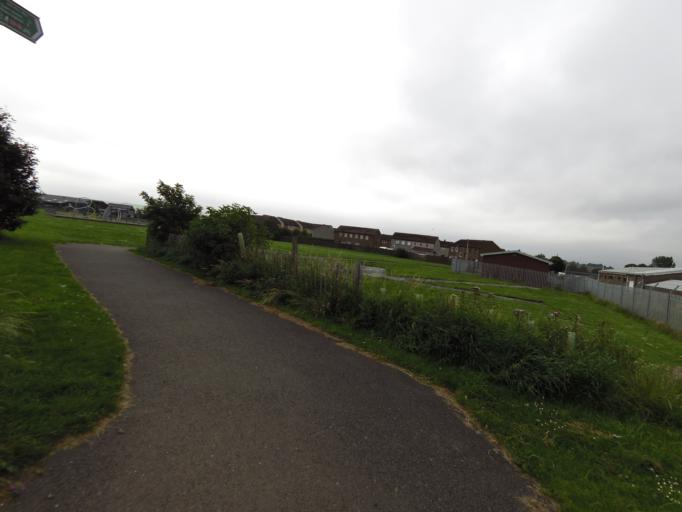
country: GB
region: Scotland
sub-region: East Lothian
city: Musselburgh
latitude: 55.9503
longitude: -3.0483
